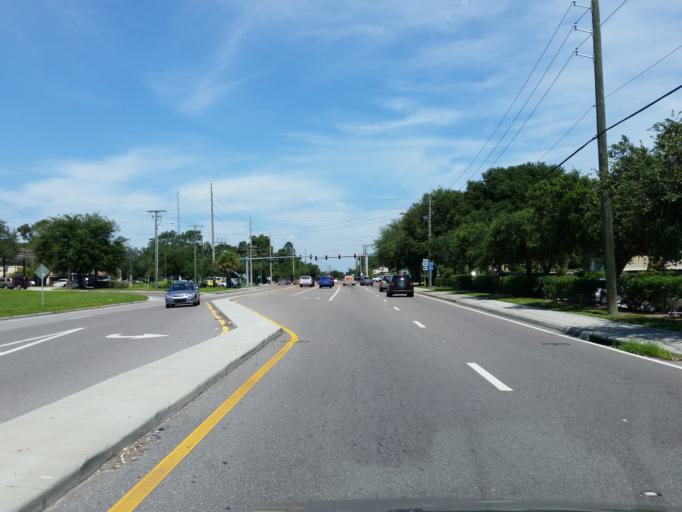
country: US
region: Florida
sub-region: Hillsborough County
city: Riverview
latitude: 27.8920
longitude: -82.3184
